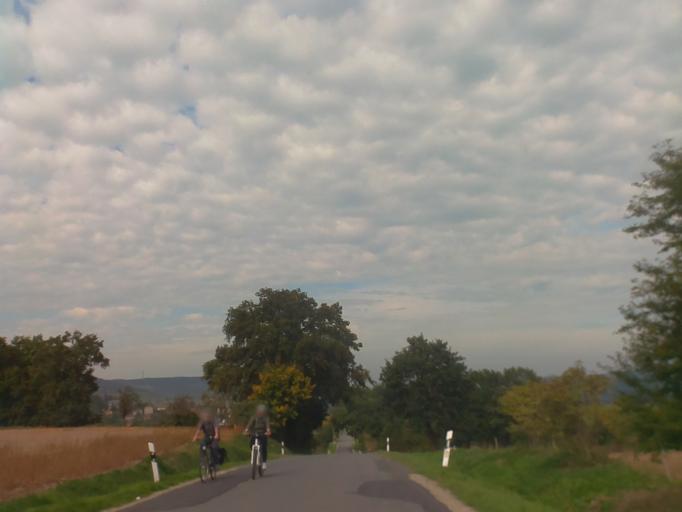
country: DE
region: Thuringia
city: Schops
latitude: 50.8399
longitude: 11.6115
